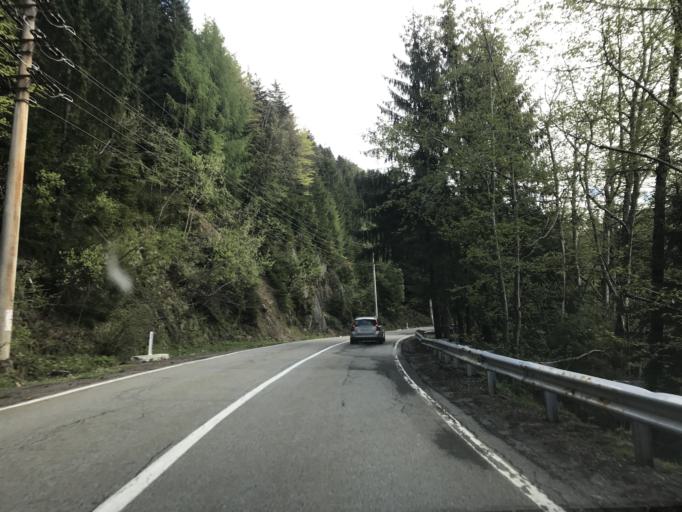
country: RO
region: Sibiu
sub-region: Comuna Cartisoara
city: Cartisoara
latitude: 45.6560
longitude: 24.6024
